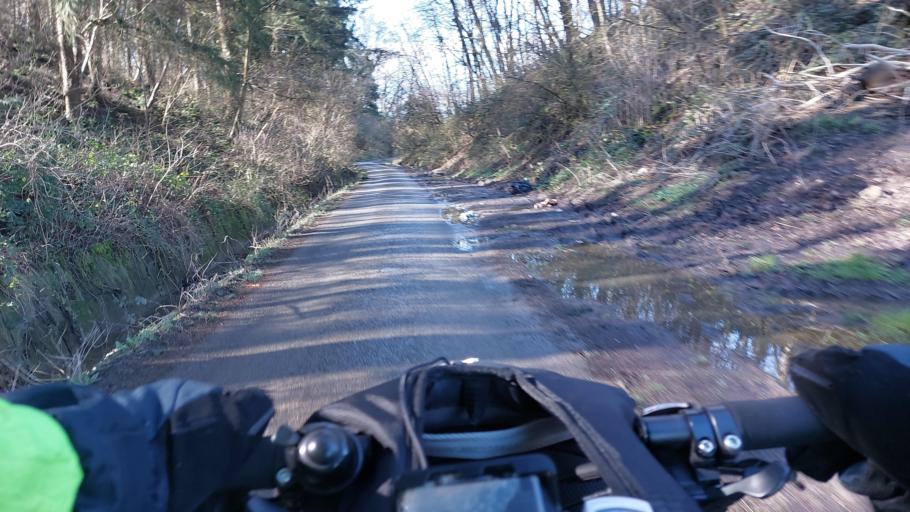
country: BE
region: Wallonia
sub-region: Province du Hainaut
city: Ecaussinnes-d'Enghien
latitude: 50.5595
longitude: 4.1991
